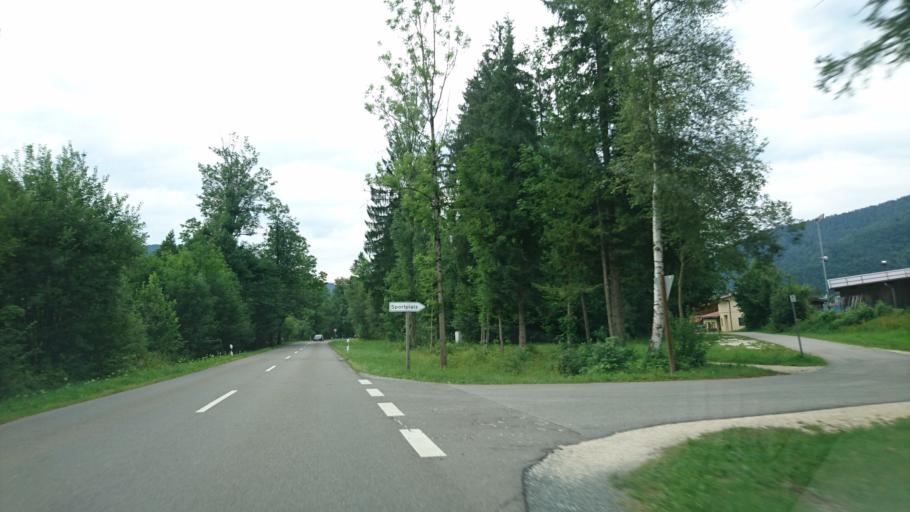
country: DE
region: Bavaria
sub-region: Upper Bavaria
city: Ruhpolding
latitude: 47.7461
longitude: 12.6563
